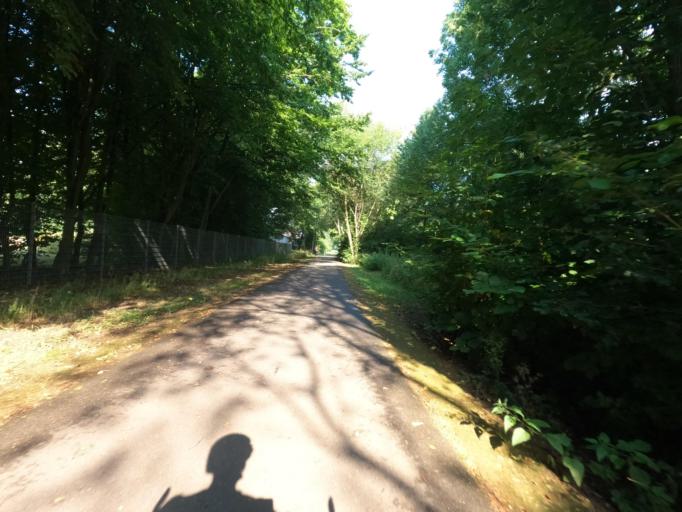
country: DE
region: North Rhine-Westphalia
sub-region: Regierungsbezirk Koln
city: Heinsberg
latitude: 51.0741
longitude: 6.0870
